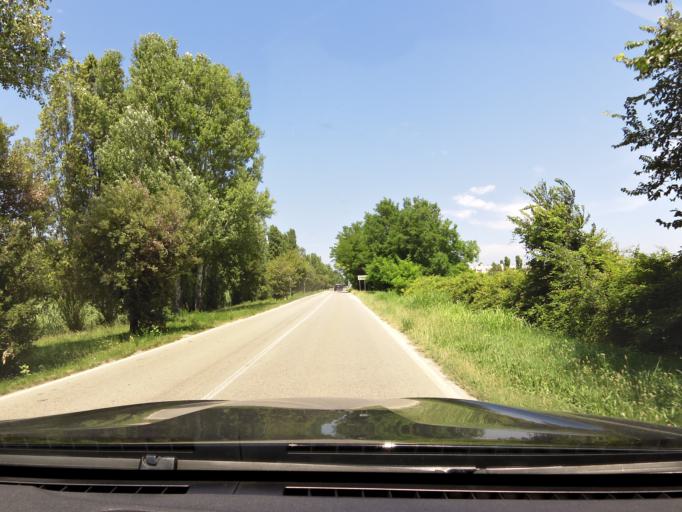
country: IT
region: The Marches
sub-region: Provincia di Pesaro e Urbino
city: Fano
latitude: 43.8266
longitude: 13.0156
